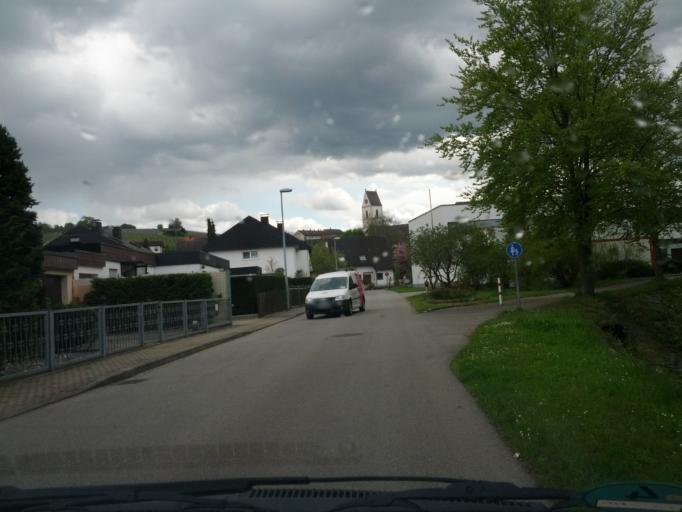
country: DE
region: Baden-Wuerttemberg
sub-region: Freiburg Region
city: Pfaffenweiler
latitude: 47.9390
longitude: 7.7534
